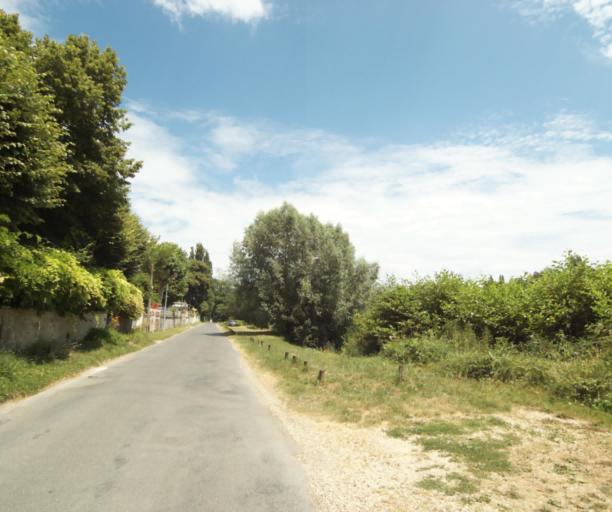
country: FR
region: Ile-de-France
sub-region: Departement de Seine-et-Marne
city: Samois-sur-Seine
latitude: 48.4450
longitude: 2.7504
